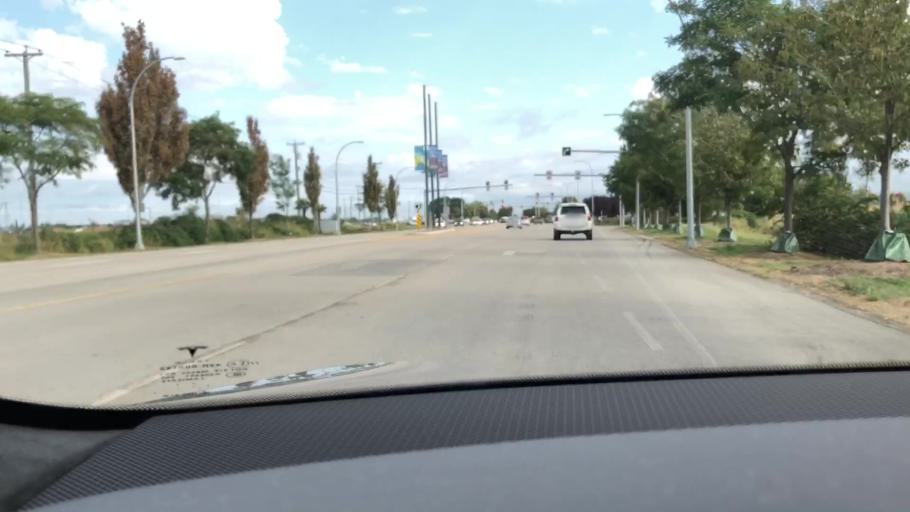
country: CA
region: British Columbia
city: Ladner
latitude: 49.0401
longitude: -123.0685
